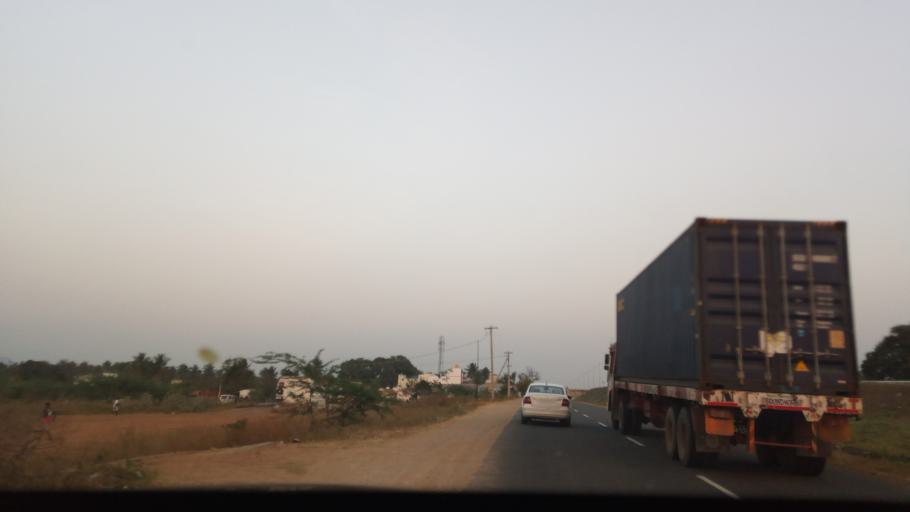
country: IN
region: Tamil Nadu
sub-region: Salem
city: Salem
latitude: 11.6642
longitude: 78.2403
